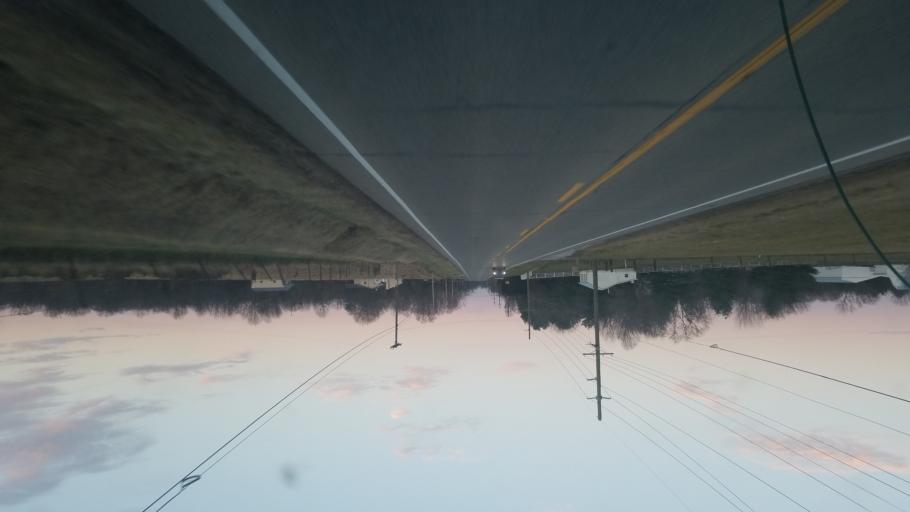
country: US
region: Indiana
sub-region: Lawrence County
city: Bedford
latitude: 38.8751
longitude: -86.3702
